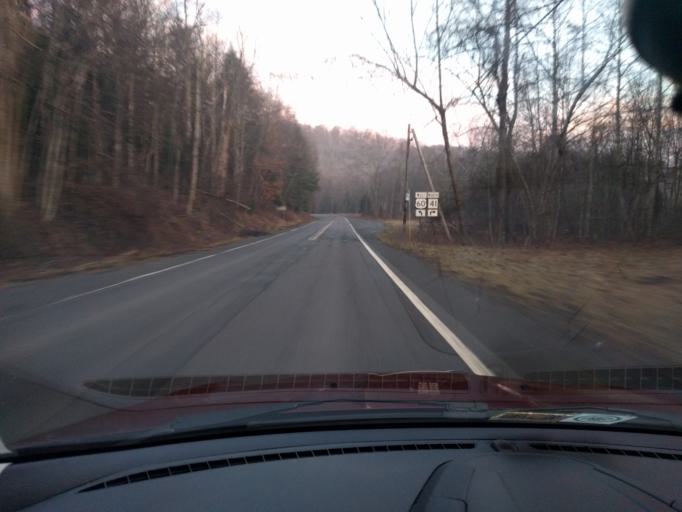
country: US
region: West Virginia
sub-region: Fayette County
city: Fayetteville
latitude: 38.0493
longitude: -80.9272
